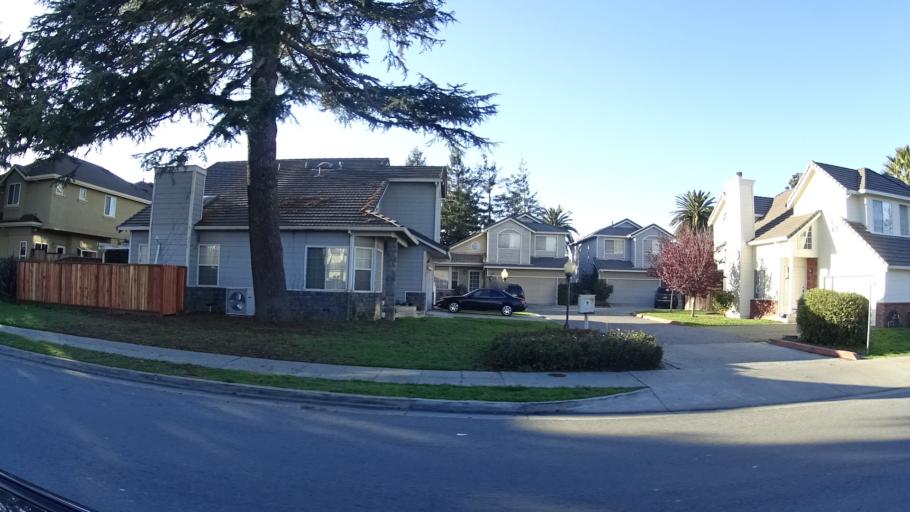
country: US
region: California
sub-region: Santa Clara County
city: Sunnyvale
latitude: 37.3790
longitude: -122.0280
